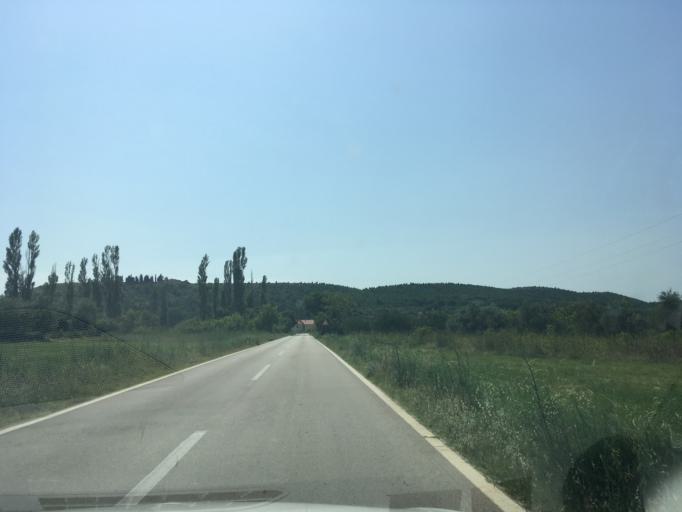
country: HR
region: Sibensko-Kniniska
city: Zaton
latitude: 43.9302
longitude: 15.8194
